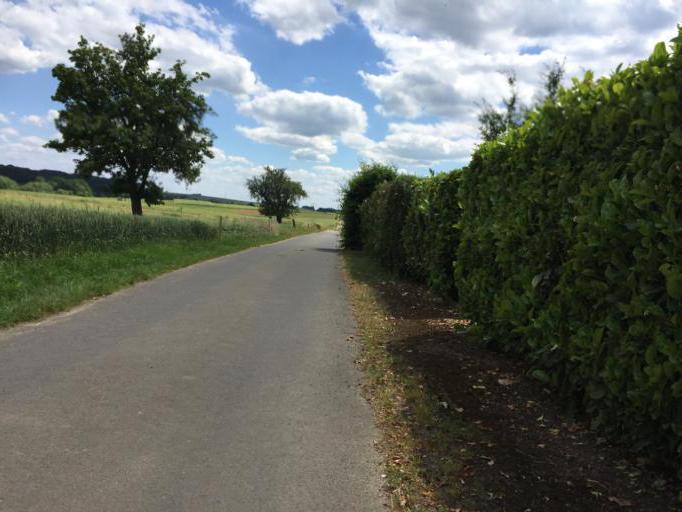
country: DE
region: Rheinland-Pfalz
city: Steinefrenz
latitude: 50.4745
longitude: 7.9236
